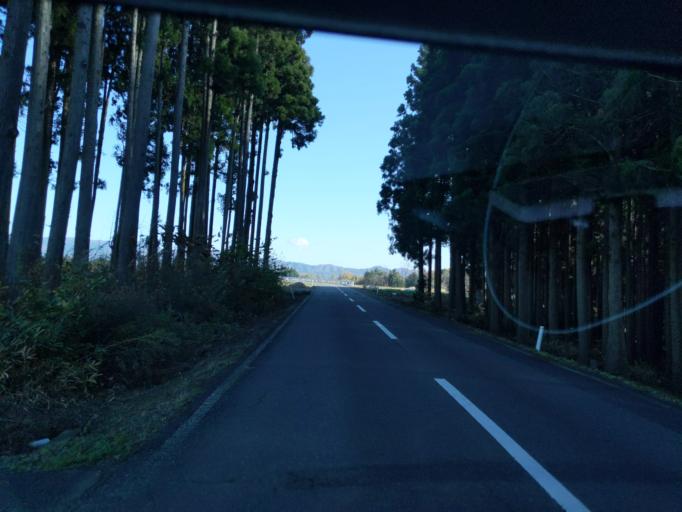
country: JP
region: Iwate
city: Mizusawa
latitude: 39.0723
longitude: 141.1154
